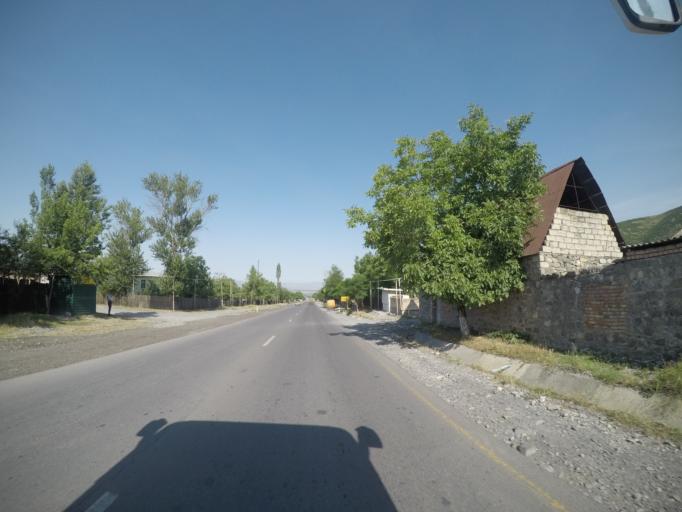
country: AZ
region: Shaki City
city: Sheki
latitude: 41.2105
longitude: 47.1398
